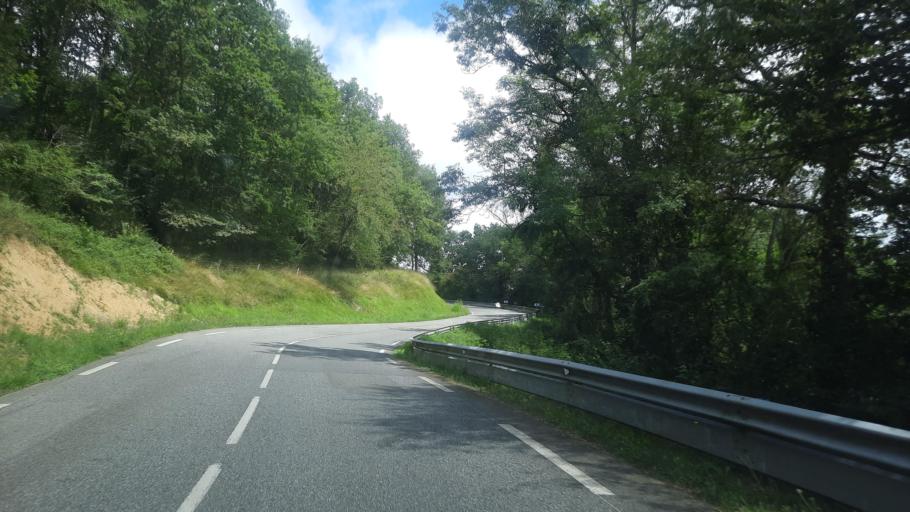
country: FR
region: Midi-Pyrenees
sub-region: Departement des Hautes-Pyrenees
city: Trie-sur-Baise
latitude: 43.2981
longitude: 0.2819
